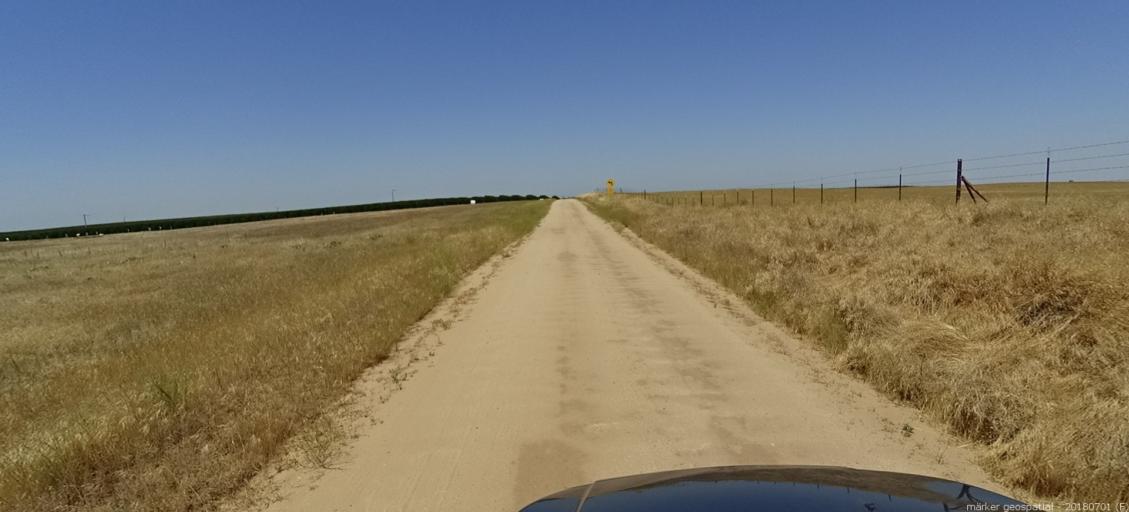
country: US
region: California
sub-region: Madera County
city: Madera Acres
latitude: 37.0977
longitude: -120.0268
